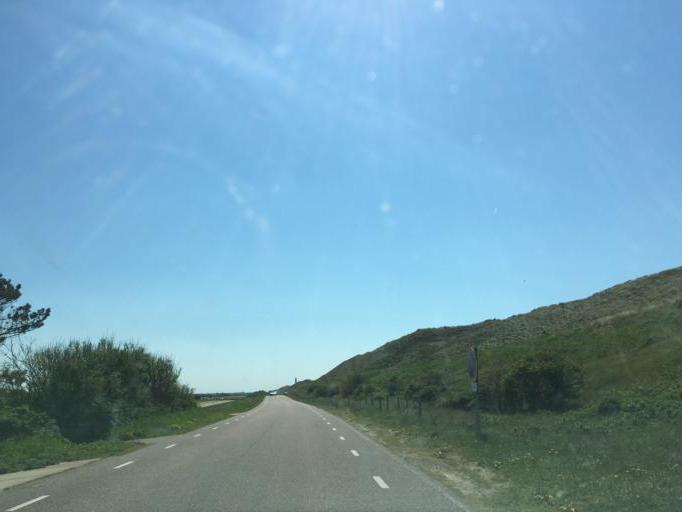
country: NL
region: North Holland
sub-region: Gemeente Den Helder
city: Den Helder
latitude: 52.8917
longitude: 4.7171
